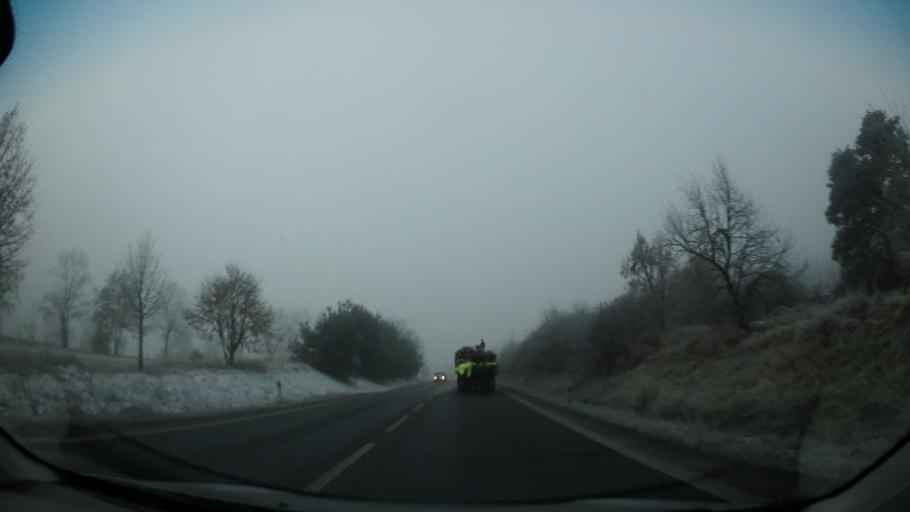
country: CZ
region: Vysocina
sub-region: Okres Trebic
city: Trebic
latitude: 49.2492
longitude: 15.9072
